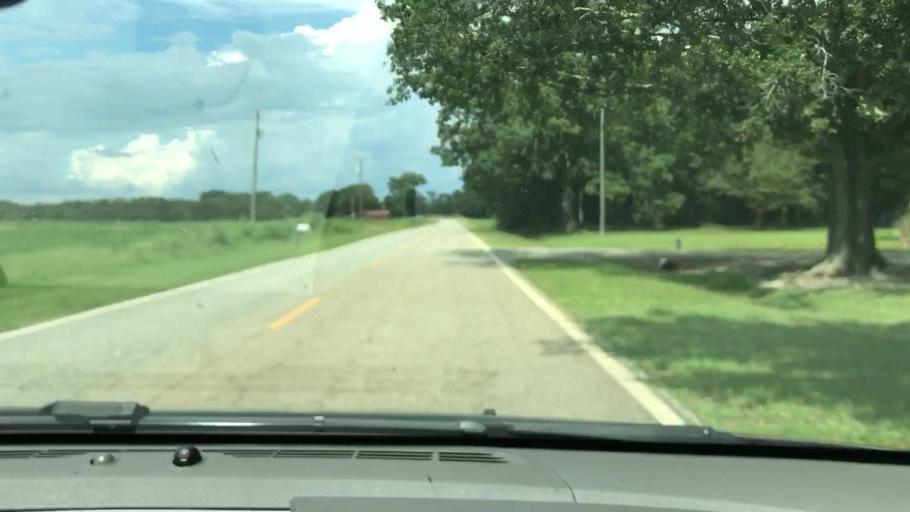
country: US
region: Georgia
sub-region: Early County
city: Blakely
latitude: 31.2273
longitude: -84.9951
